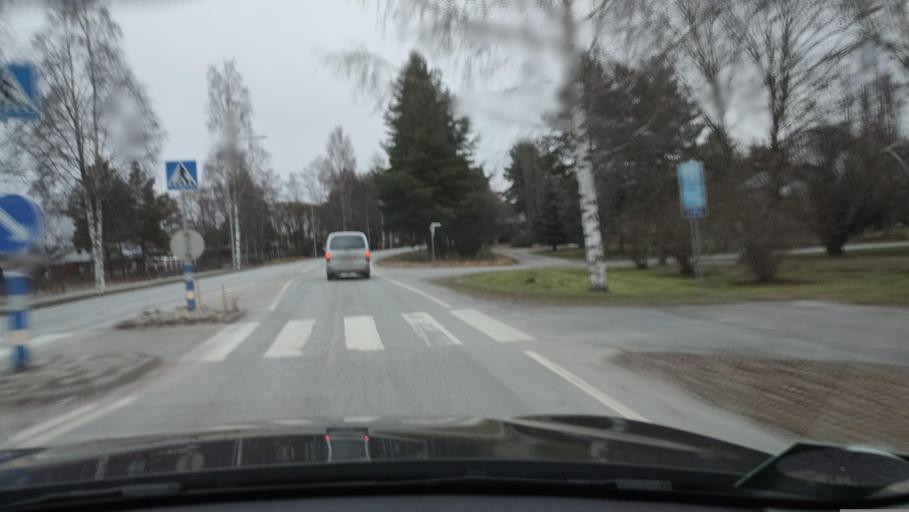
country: FI
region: Southern Ostrobothnia
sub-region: Suupohja
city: Kauhajoki
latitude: 62.4364
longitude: 22.1877
